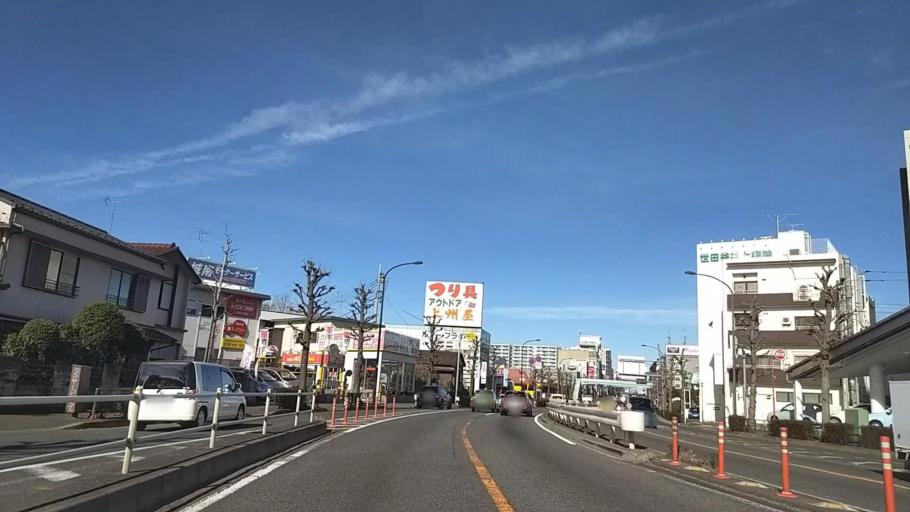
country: JP
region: Tokyo
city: Chofugaoka
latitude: 35.6382
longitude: 139.6201
